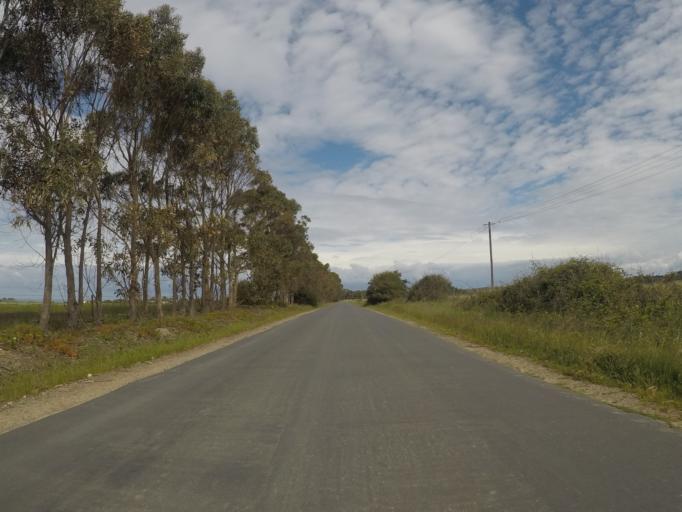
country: PT
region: Beja
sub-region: Odemira
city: Sao Teotonio
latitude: 37.4915
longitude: -8.7818
